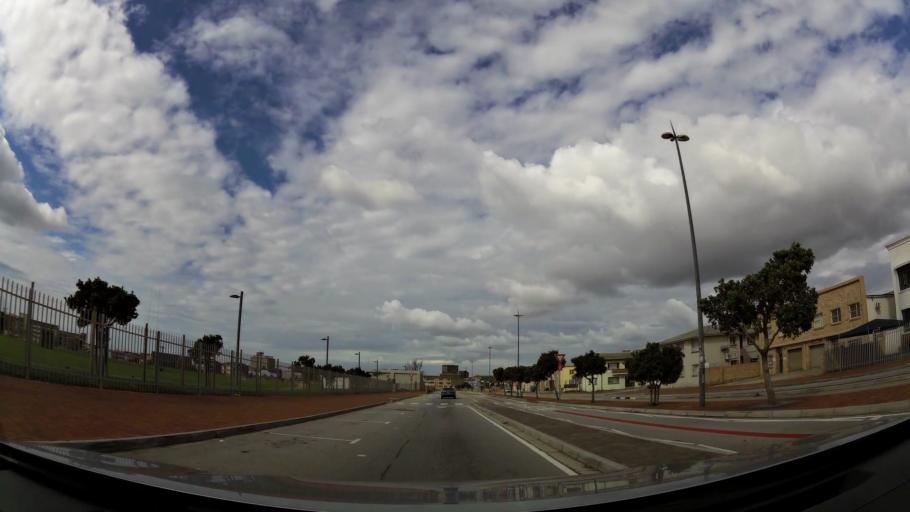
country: ZA
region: Eastern Cape
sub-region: Nelson Mandela Bay Metropolitan Municipality
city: Port Elizabeth
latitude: -33.9405
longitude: 25.5998
